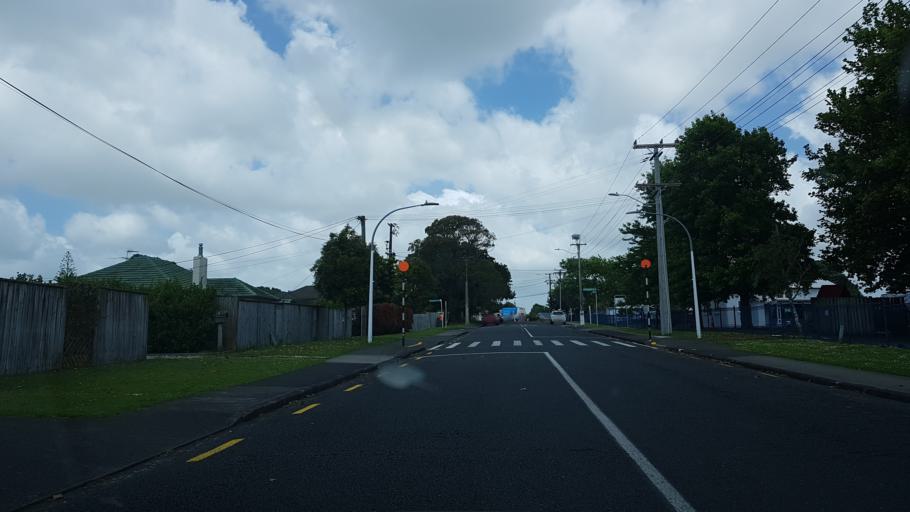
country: NZ
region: Auckland
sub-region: Auckland
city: North Shore
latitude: -36.7997
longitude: 174.7042
